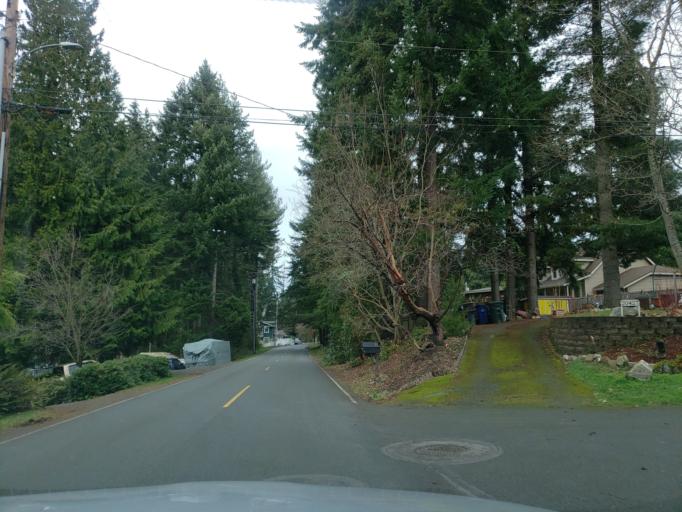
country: US
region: Washington
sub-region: Snohomish County
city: Esperance
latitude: 47.8131
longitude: -122.3441
